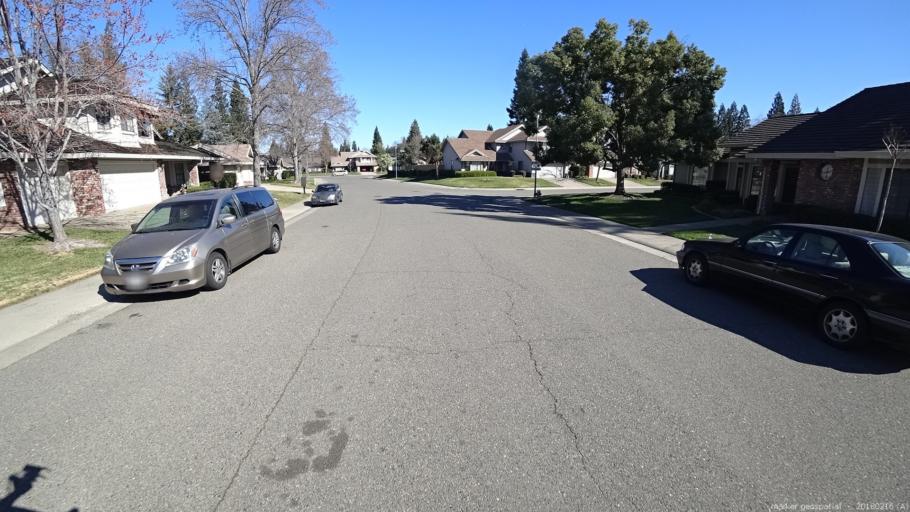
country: US
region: California
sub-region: Sacramento County
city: Gold River
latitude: 38.6217
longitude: -121.2470
